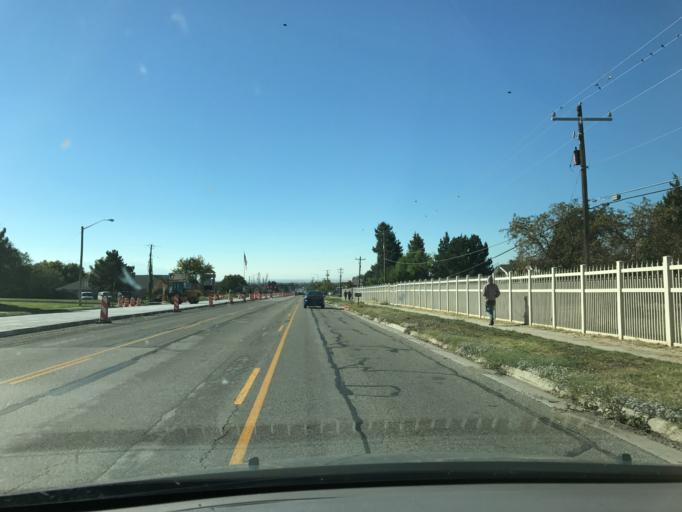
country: US
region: Utah
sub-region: Davis County
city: Hill Air Force Bace
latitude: 41.0928
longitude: -111.9736
